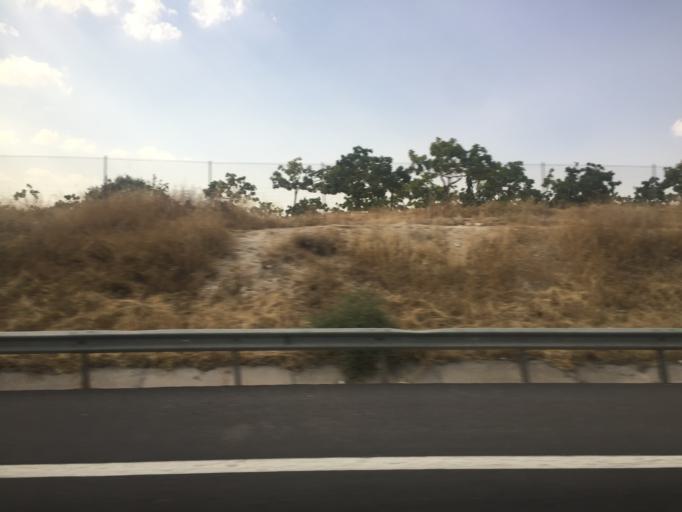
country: TR
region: Sanliurfa
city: Akziyaret
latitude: 37.2709
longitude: 38.7997
